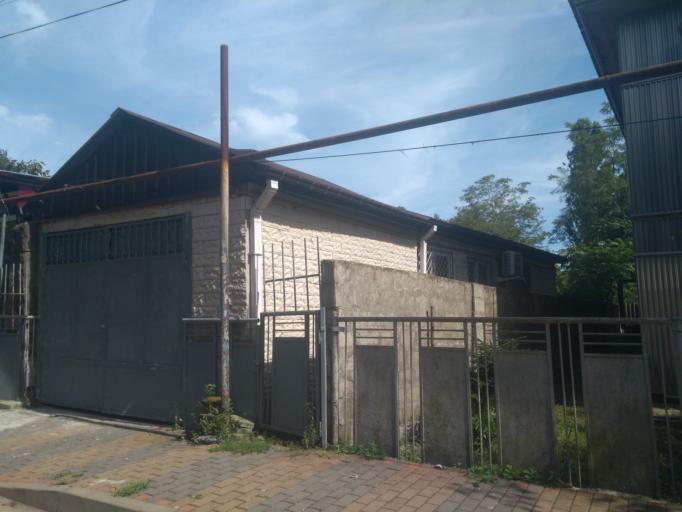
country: GE
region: Ajaria
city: Kobuleti
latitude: 41.8637
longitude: 41.7832
